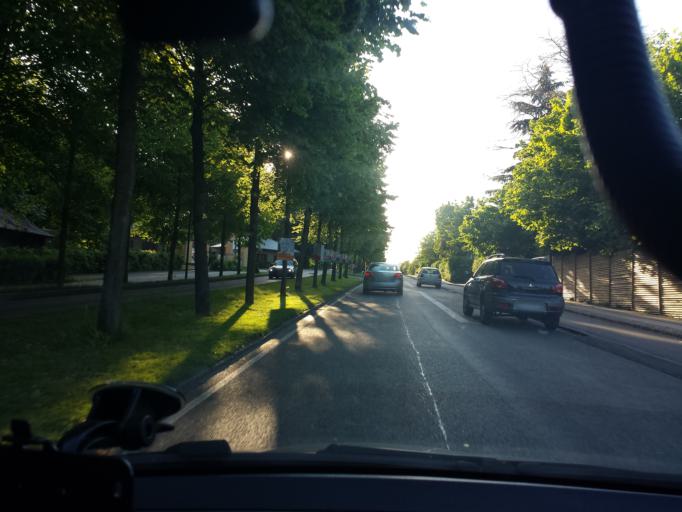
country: DK
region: Capital Region
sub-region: Gentofte Kommune
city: Charlottenlund
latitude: 55.7590
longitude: 12.5561
